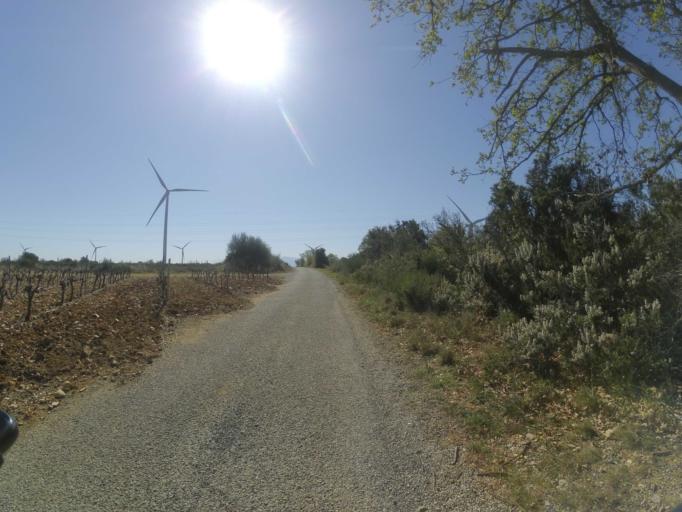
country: FR
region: Languedoc-Roussillon
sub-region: Departement des Pyrenees-Orientales
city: Pezilla-la-Riviere
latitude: 42.7191
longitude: 2.7707
